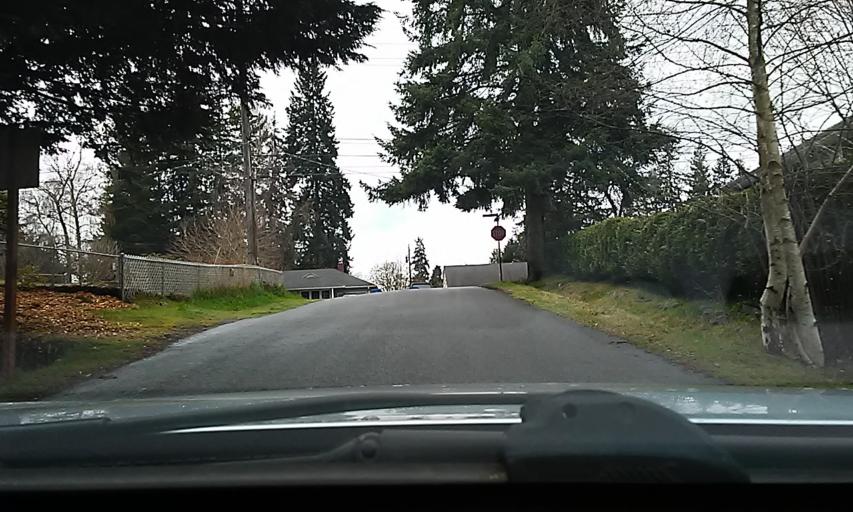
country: US
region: Washington
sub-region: King County
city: Shoreline
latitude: 47.7459
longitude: -122.3394
